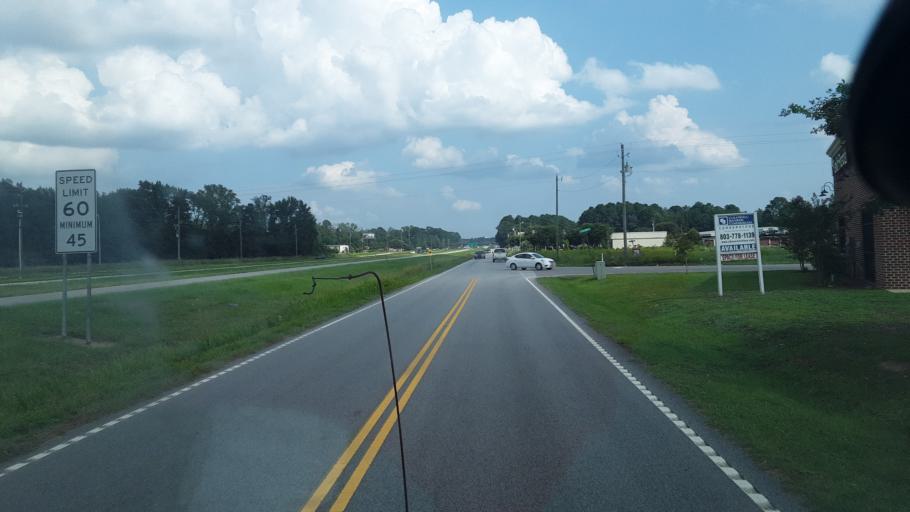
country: US
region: South Carolina
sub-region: Sumter County
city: Sumter
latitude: 33.9556
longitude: -80.3720
